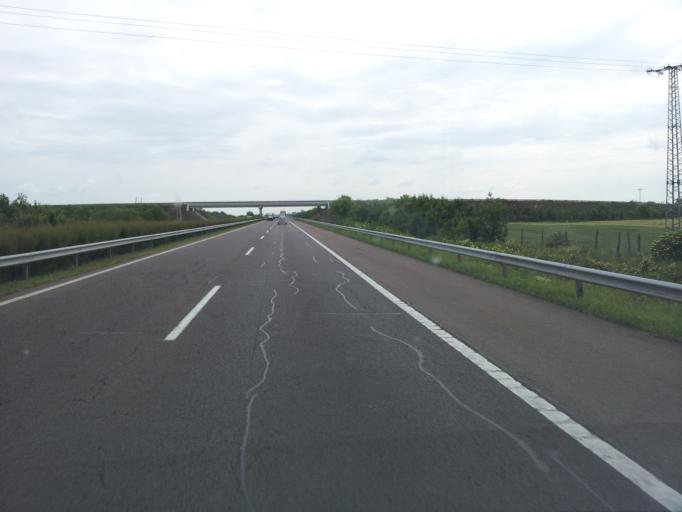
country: HU
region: Heves
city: Szihalom
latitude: 47.7606
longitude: 20.4964
